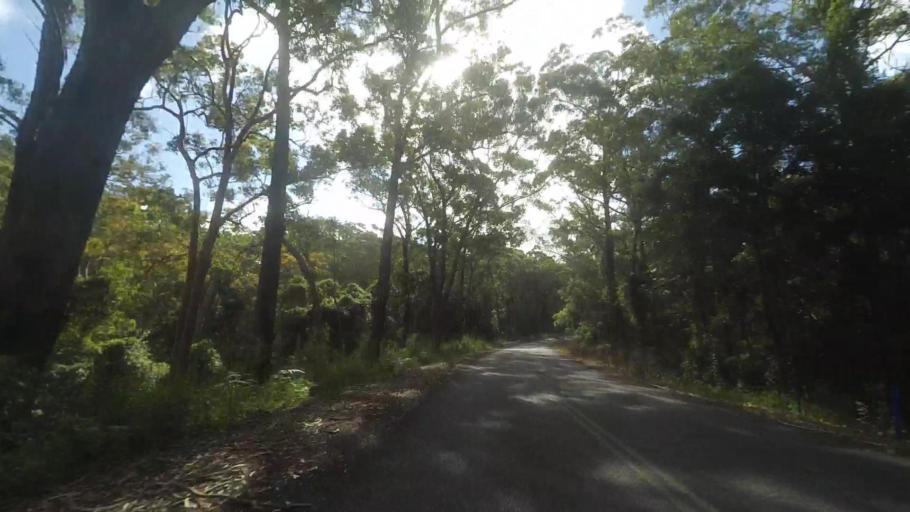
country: AU
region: New South Wales
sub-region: Great Lakes
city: Forster
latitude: -32.4294
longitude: 152.5060
